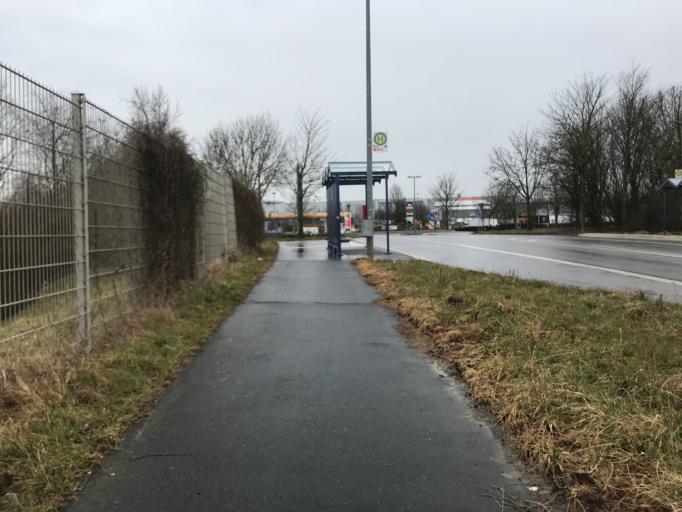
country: DE
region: Rheinland-Pfalz
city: Ober-Olm
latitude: 49.9147
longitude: 8.1764
